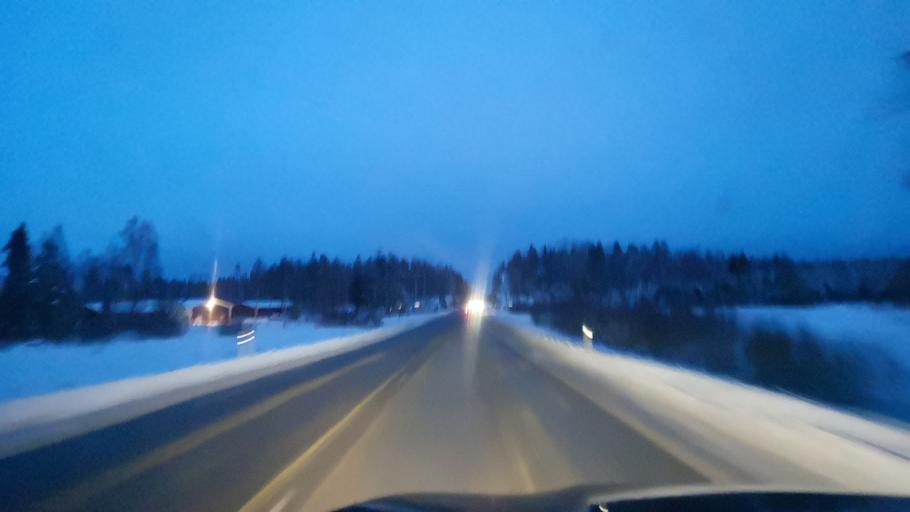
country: FI
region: Varsinais-Suomi
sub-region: Loimaa
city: Loimaa
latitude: 60.8732
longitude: 23.0649
